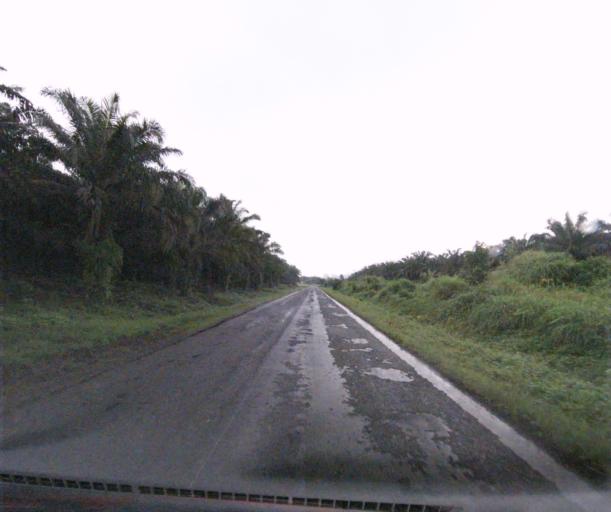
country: CM
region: South-West Province
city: Idenao
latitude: 4.1146
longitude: 8.9903
